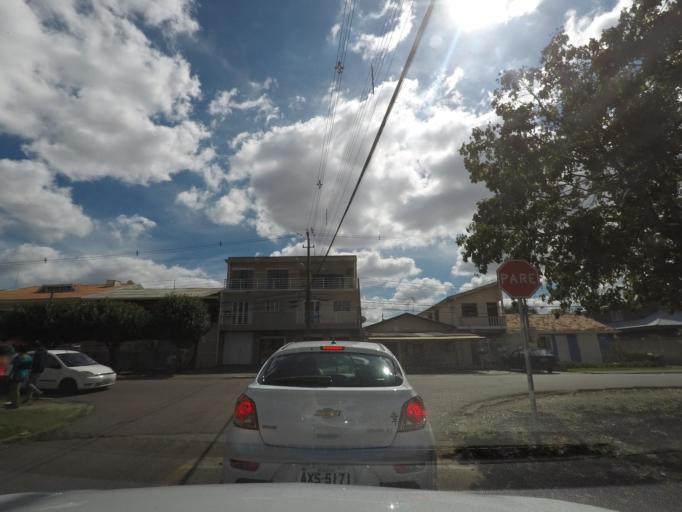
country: BR
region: Parana
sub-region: Sao Jose Dos Pinhais
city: Sao Jose dos Pinhais
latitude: -25.5048
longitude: -49.2189
